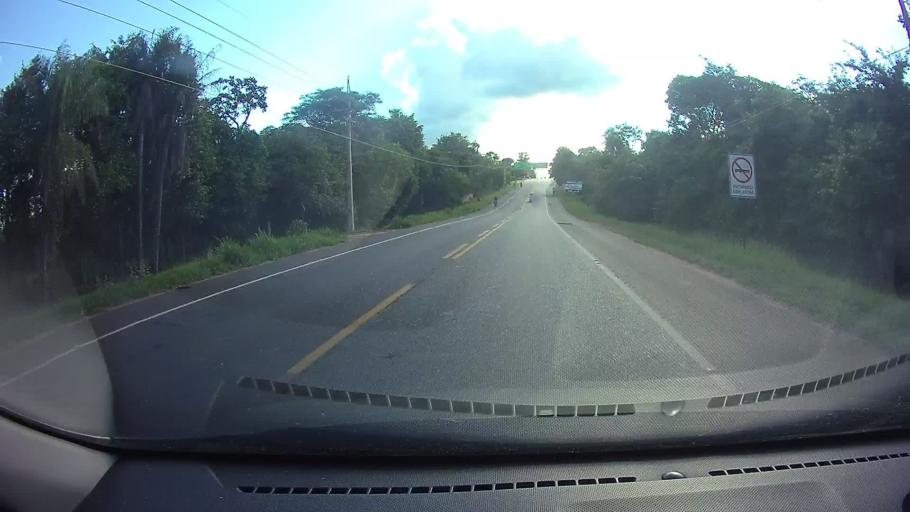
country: PY
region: Cordillera
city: Eusebio Ayala
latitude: -25.3811
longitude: -57.0412
